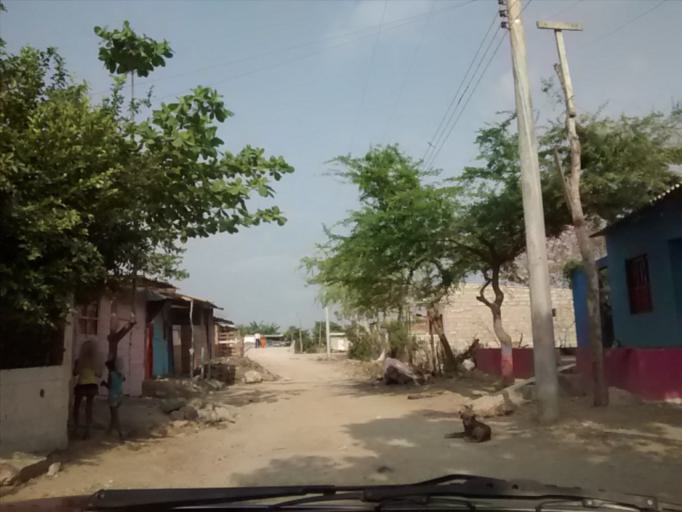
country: CO
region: Bolivar
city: Cartagena
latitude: 10.4162
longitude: -75.4655
